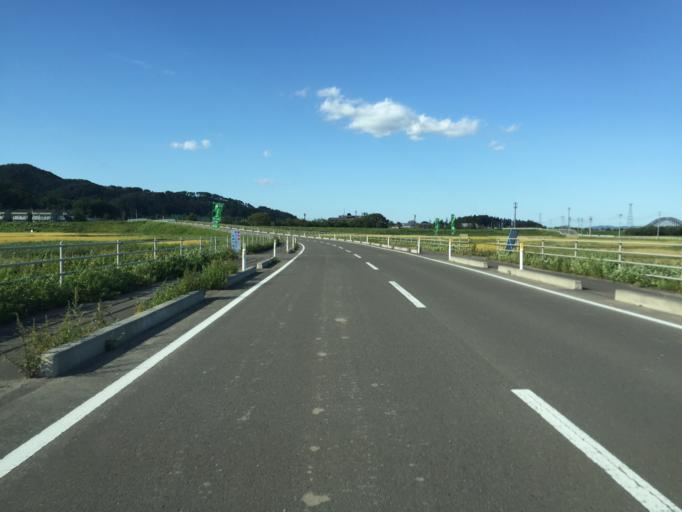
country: JP
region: Miyagi
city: Marumori
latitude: 37.9044
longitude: 140.7659
